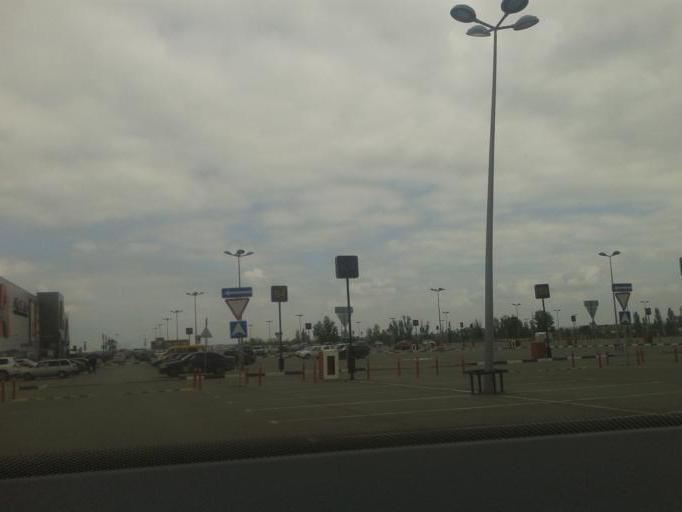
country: RU
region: Volgograd
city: Volgograd
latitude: 48.6354
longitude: 44.4331
